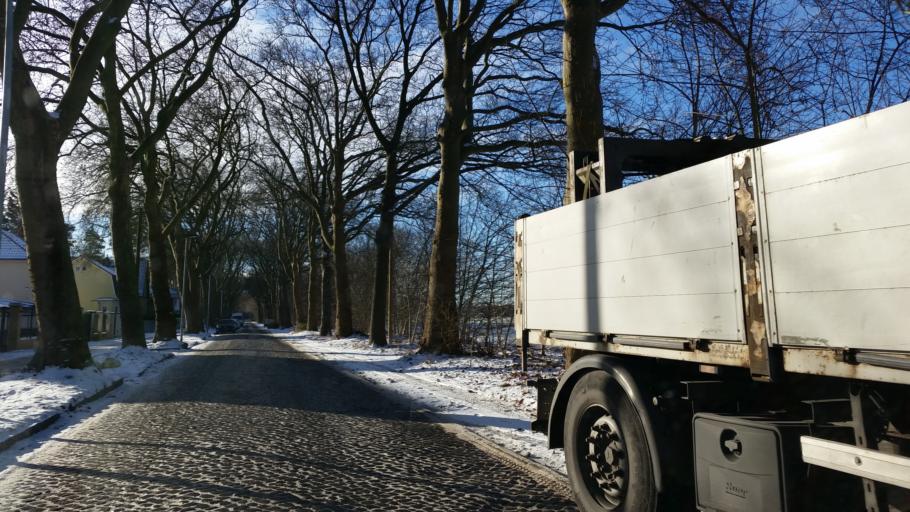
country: DE
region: Berlin
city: Lichtenrade
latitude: 52.3745
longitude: 13.4175
